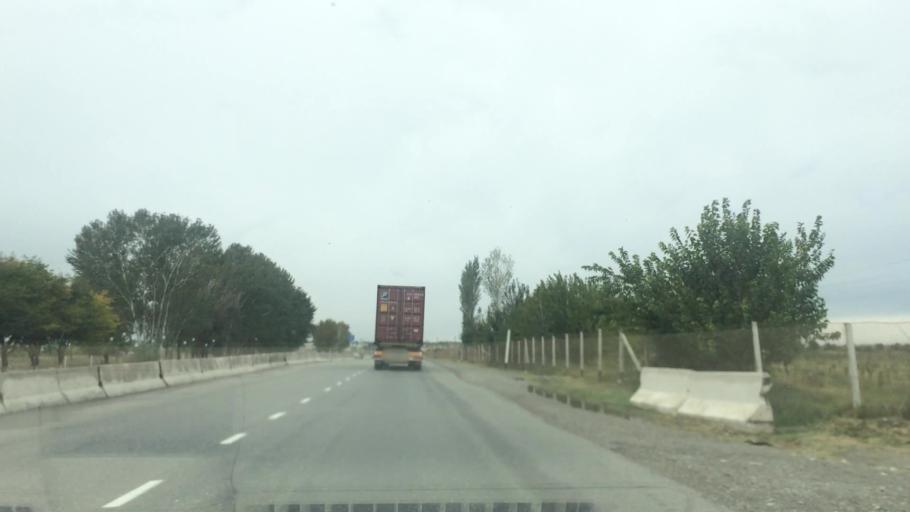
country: UZ
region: Samarqand
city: Bulung'ur
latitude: 39.7797
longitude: 67.2948
